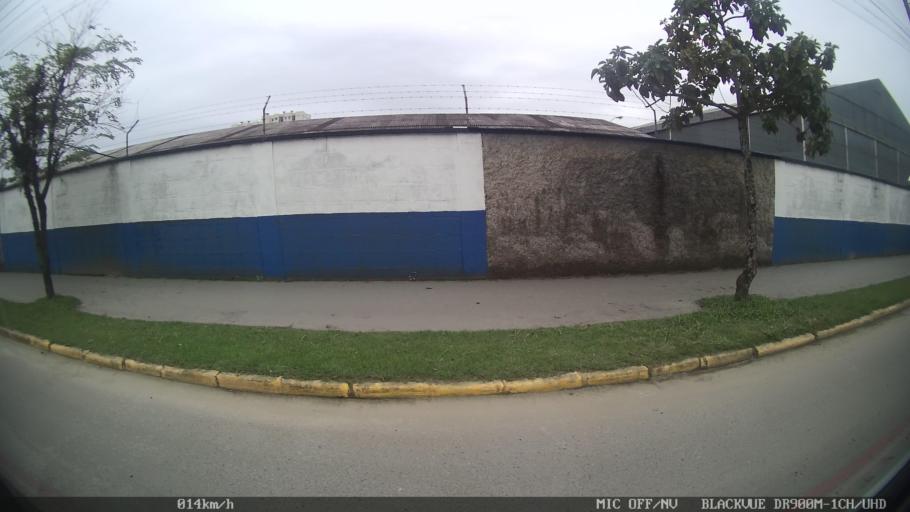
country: BR
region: Santa Catarina
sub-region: Joinville
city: Joinville
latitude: -26.3141
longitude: -48.8334
